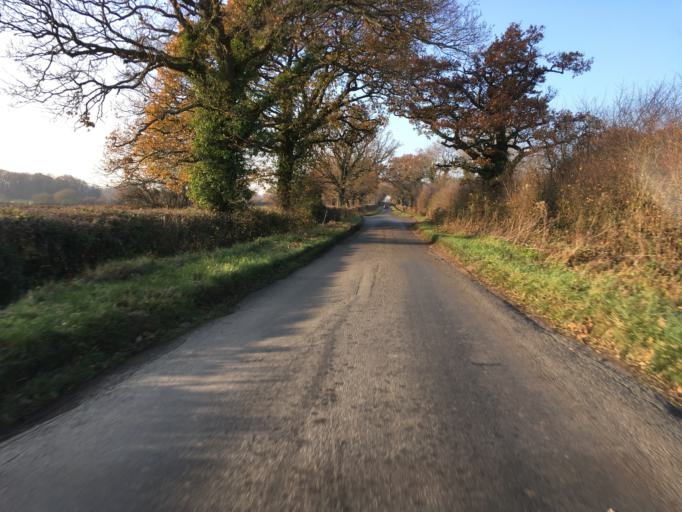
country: GB
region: England
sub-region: South Gloucestershire
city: Chipping Sodbury
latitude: 51.5654
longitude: -2.3837
